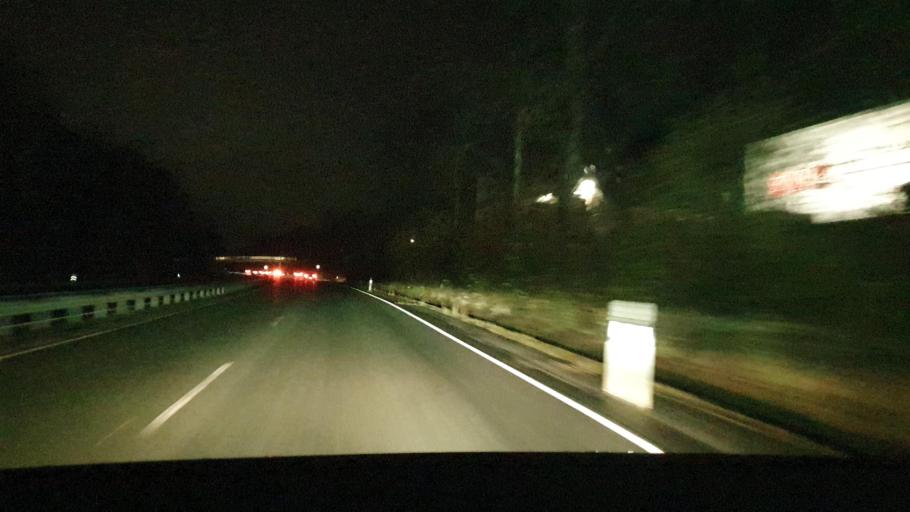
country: DE
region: North Rhine-Westphalia
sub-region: Regierungsbezirk Arnsberg
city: Siegen
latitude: 50.8844
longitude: 7.9731
